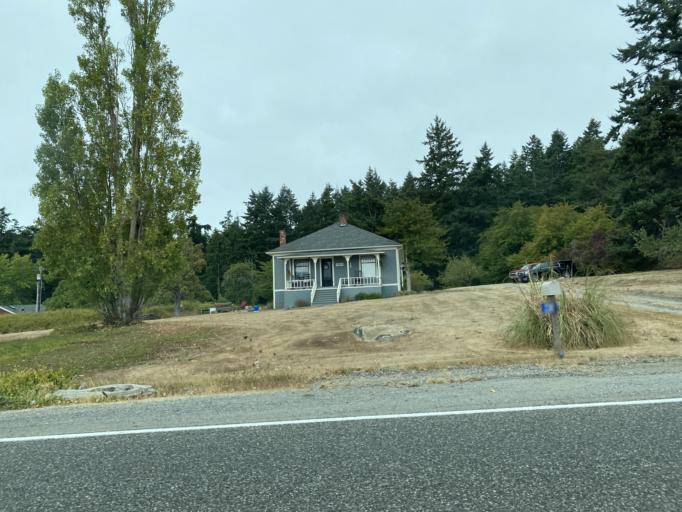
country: US
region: Washington
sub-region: Island County
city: Coupeville
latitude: 48.2288
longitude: -122.7349
